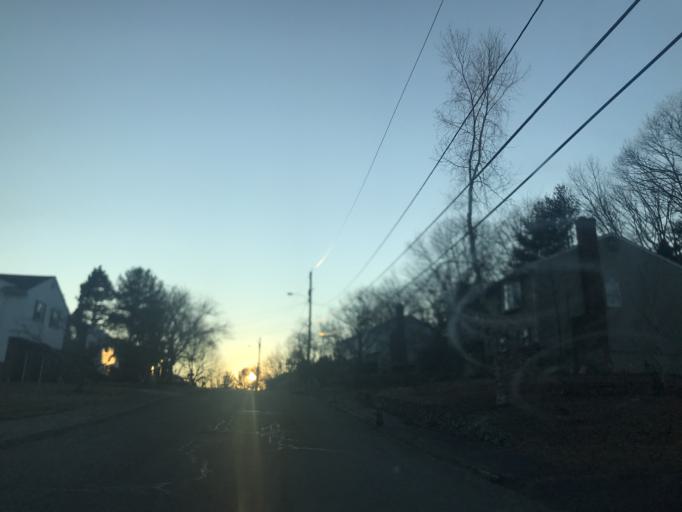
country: US
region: Massachusetts
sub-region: Essex County
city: Saugus
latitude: 42.4790
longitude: -71.0153
